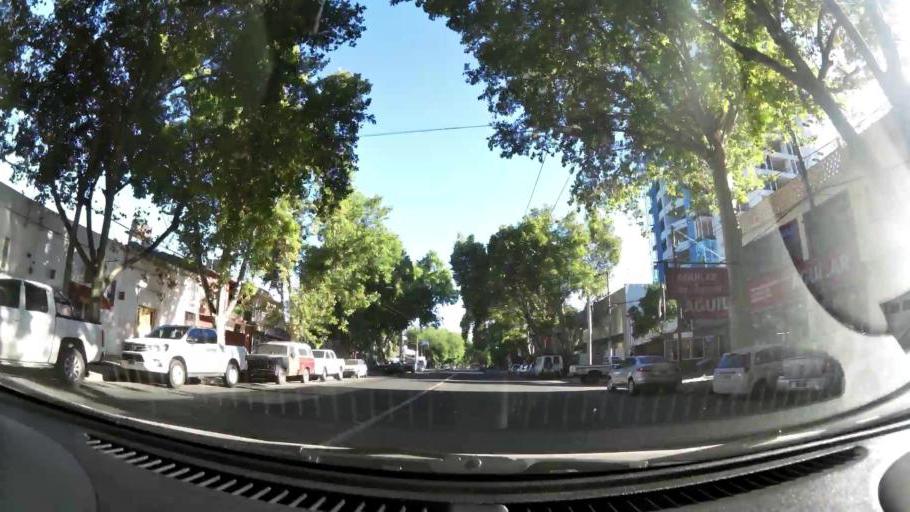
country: AR
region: Mendoza
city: Mendoza
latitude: -32.8729
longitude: -68.8348
